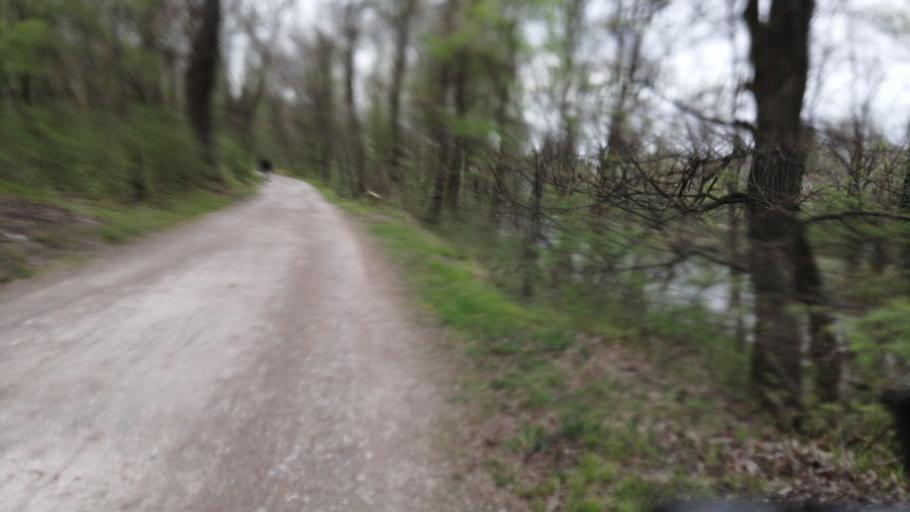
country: DE
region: Bavaria
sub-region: Upper Bavaria
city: Unterfoehring
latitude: 48.1919
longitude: 11.6346
